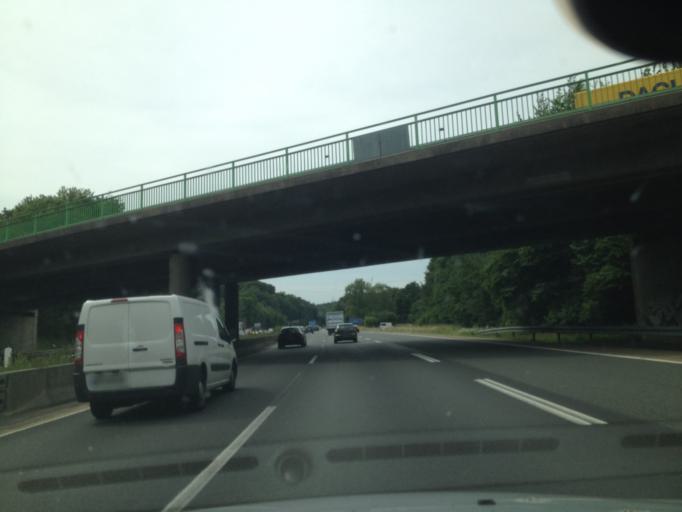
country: DE
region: North Rhine-Westphalia
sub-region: Regierungsbezirk Arnsberg
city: Luedenscheid
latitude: 51.2318
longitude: 7.6594
